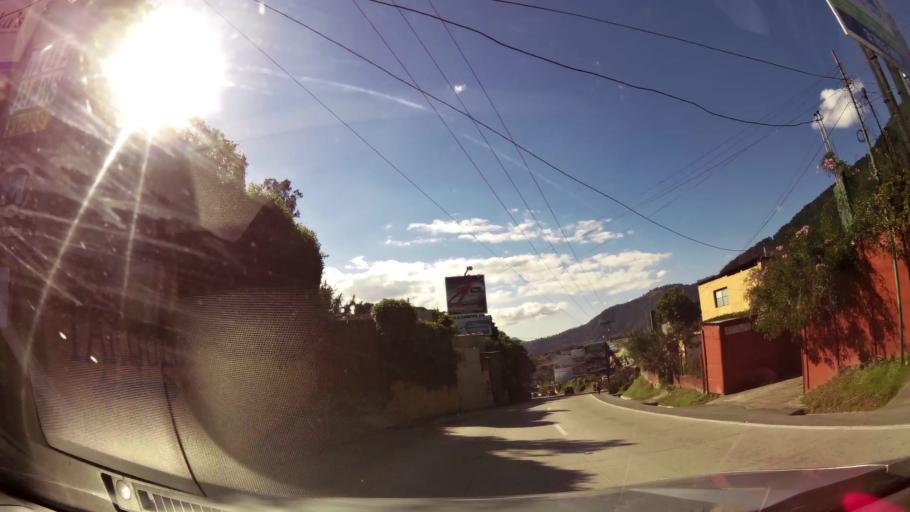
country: GT
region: Sacatepequez
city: Santa Lucia Milpas Altas
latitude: 14.5773
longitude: -90.6778
